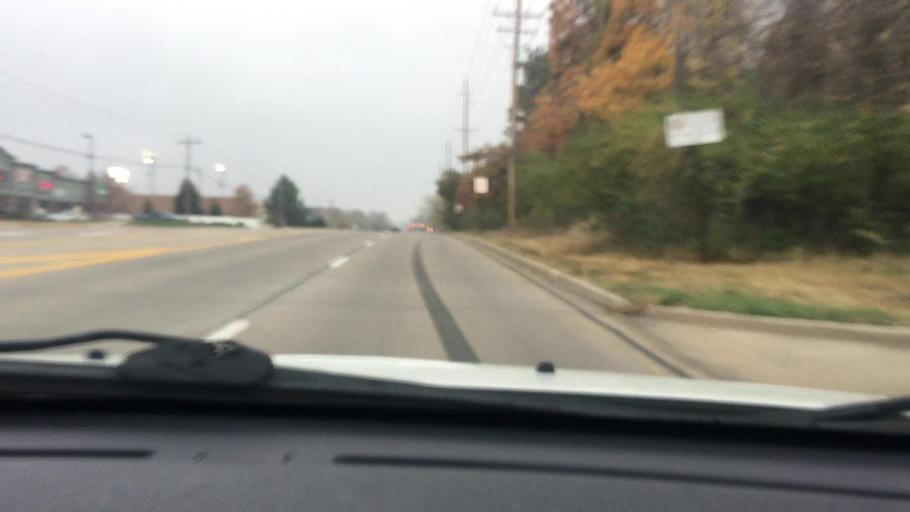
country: US
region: Missouri
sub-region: Saint Charles County
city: O'Fallon
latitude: 38.8217
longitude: -90.6762
